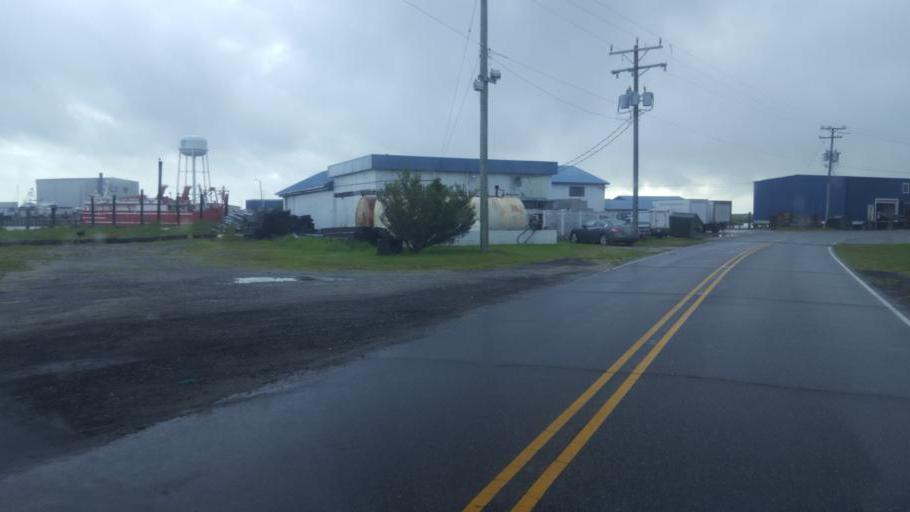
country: US
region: North Carolina
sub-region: Dare County
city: Wanchese
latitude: 35.8412
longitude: -75.6221
